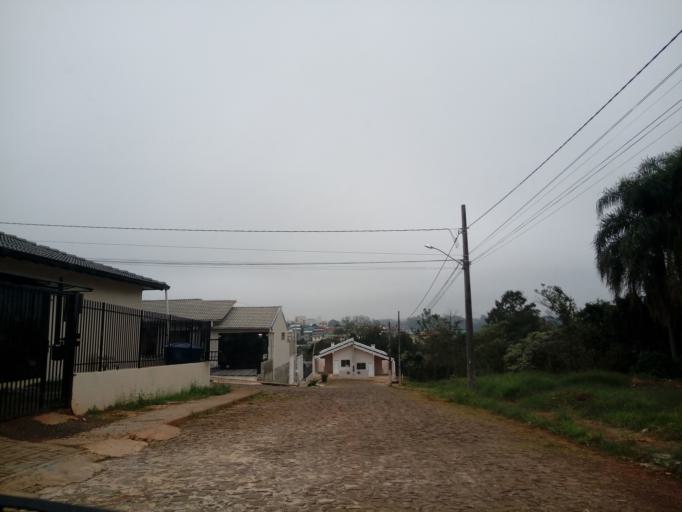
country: BR
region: Santa Catarina
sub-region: Chapeco
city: Chapeco
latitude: -27.1068
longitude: -52.6686
